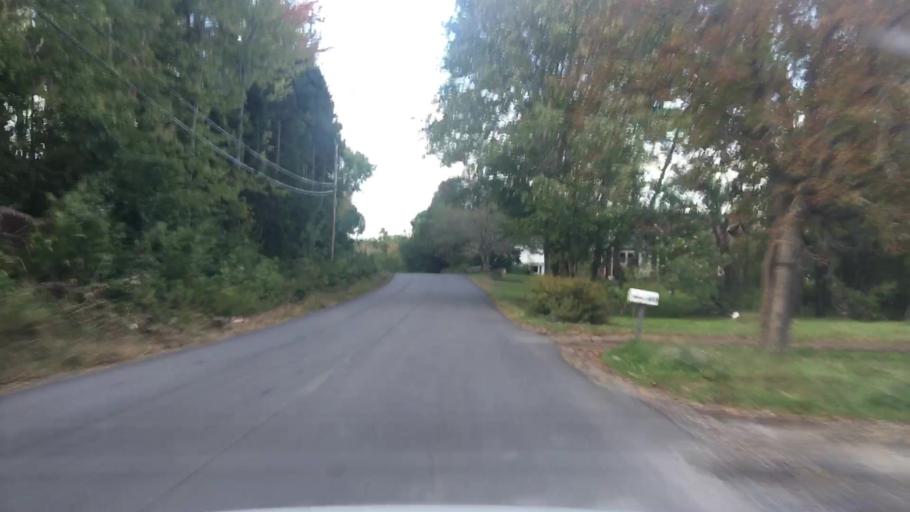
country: US
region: Maine
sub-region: Lincoln County
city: Boothbay
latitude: 43.9023
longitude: -69.6550
